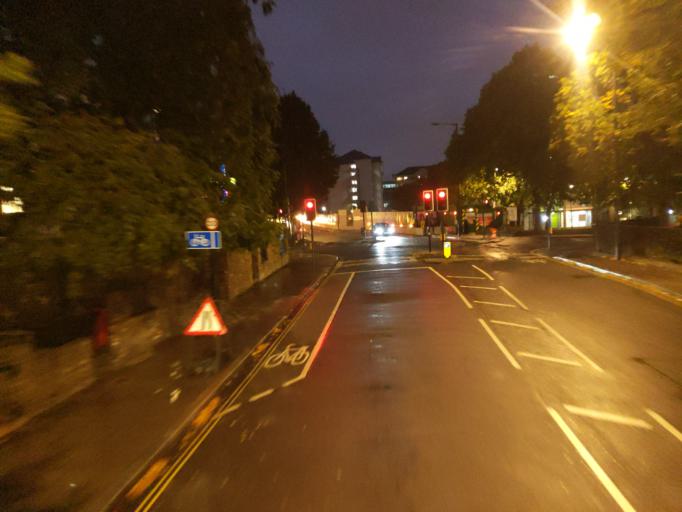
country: GB
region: England
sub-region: Greater London
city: Bayswater
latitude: 51.5245
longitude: -0.1679
